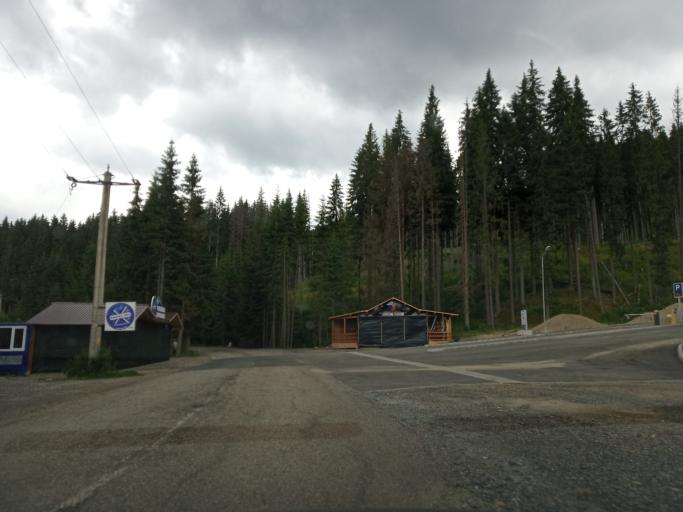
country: RO
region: Gorj
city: Novaci-Straini
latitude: 45.4173
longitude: 23.7066
